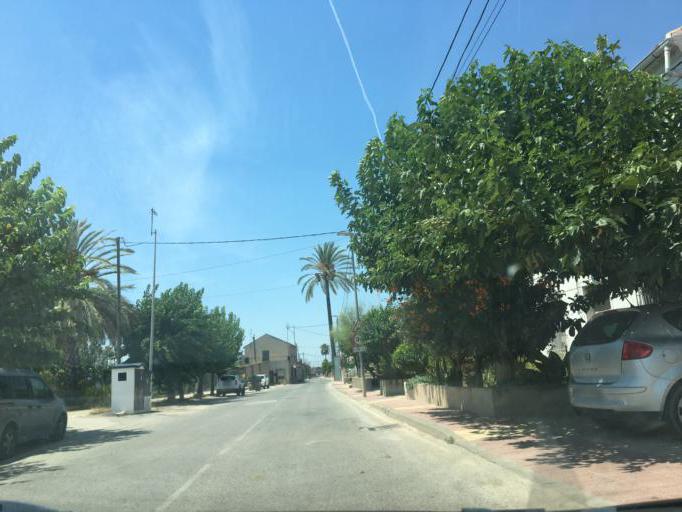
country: ES
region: Murcia
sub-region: Murcia
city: Santomera
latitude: 38.0355
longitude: -1.0565
